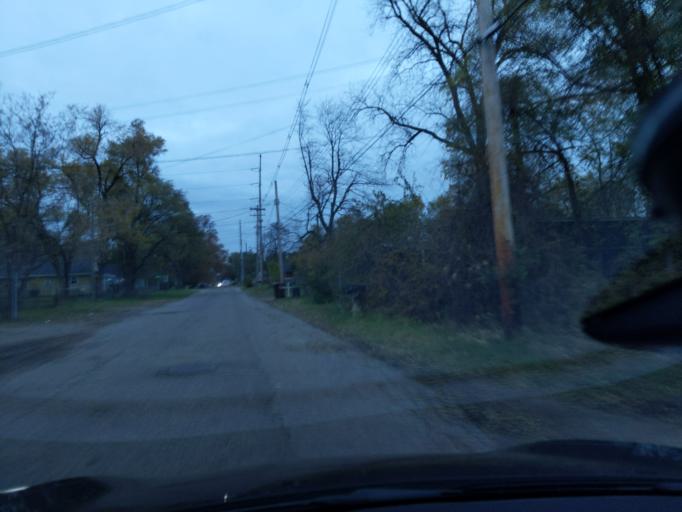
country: US
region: Michigan
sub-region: Ingham County
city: East Lansing
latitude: 42.7277
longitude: -84.5125
